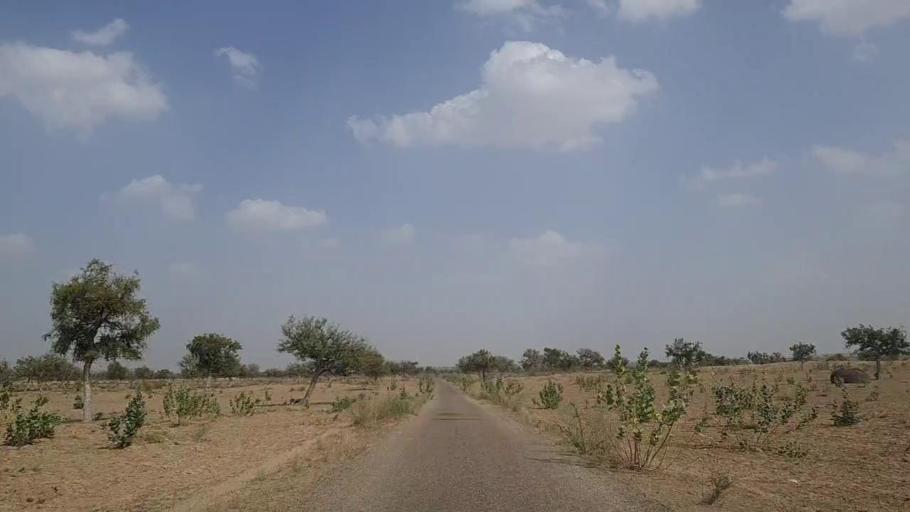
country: PK
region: Sindh
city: Islamkot
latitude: 24.8300
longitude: 70.1588
